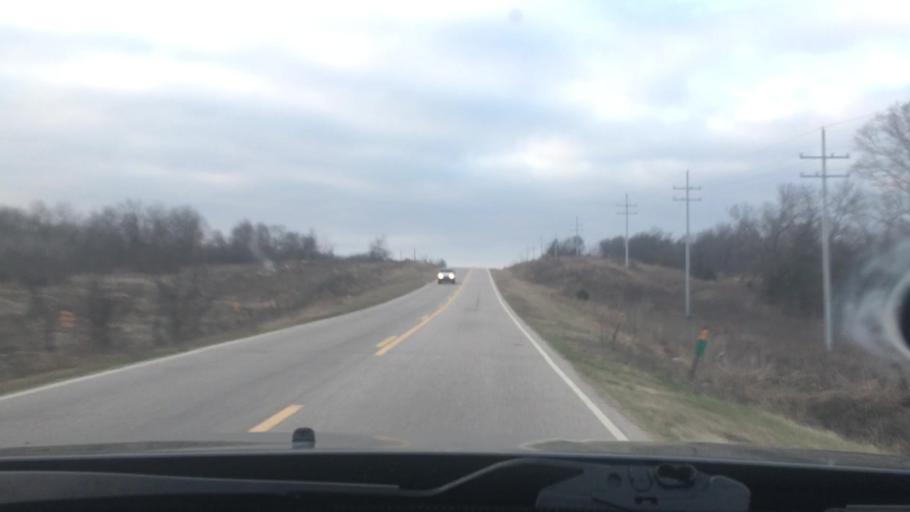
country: US
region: Oklahoma
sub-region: Pontotoc County
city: Ada
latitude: 34.6276
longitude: -96.6349
